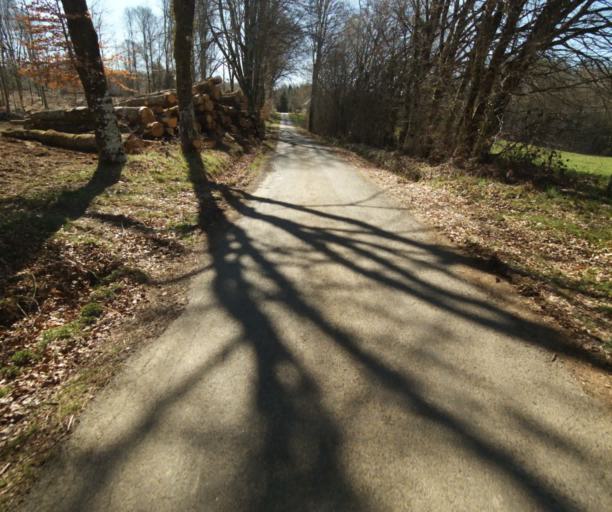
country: FR
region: Limousin
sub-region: Departement de la Correze
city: Chamboulive
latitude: 45.4200
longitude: 1.7192
